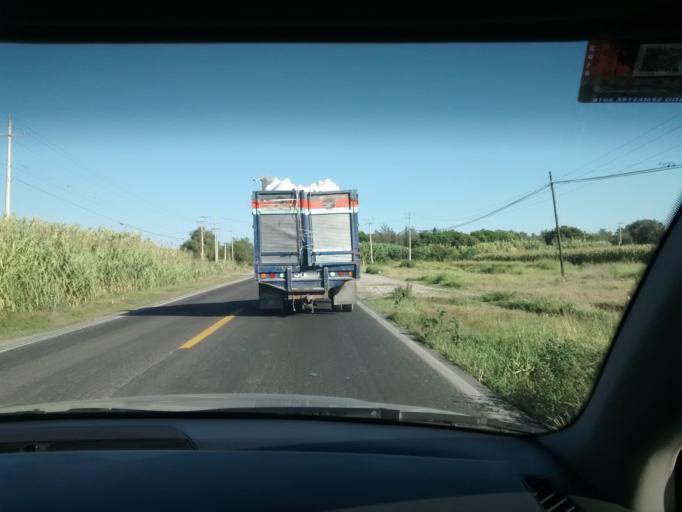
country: MX
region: Puebla
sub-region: Tehuacan
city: Magdalena Cuayucatepec
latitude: 18.5278
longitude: -97.5174
